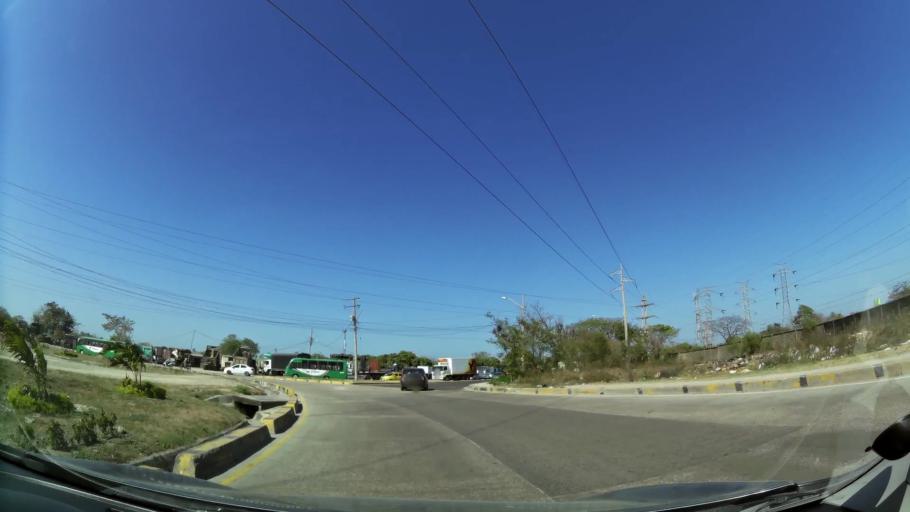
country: CO
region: Atlantico
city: Soledad
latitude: 10.9315
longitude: -74.7829
